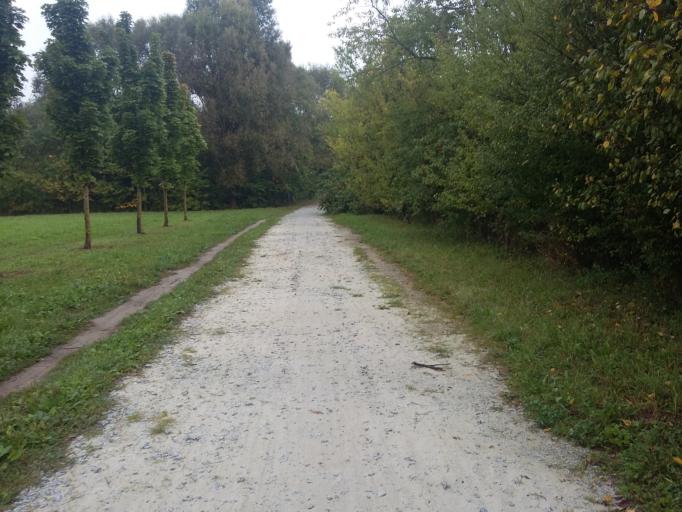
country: PL
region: Lodz Voivodeship
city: Lodz
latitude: 51.7534
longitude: 19.3973
